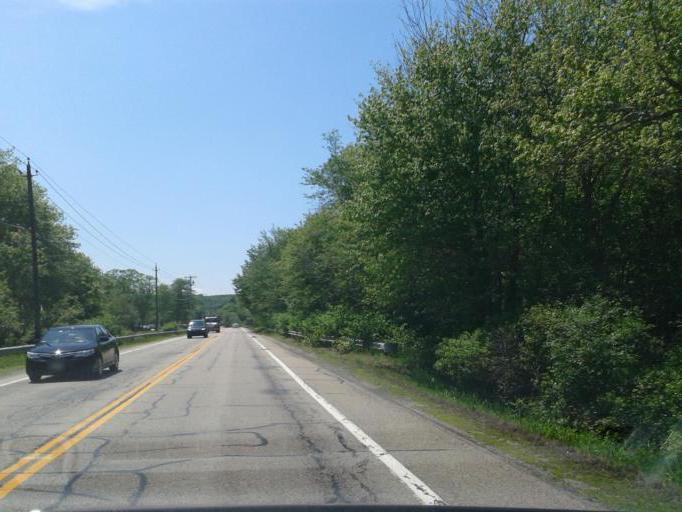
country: US
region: Rhode Island
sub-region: Washington County
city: Kingston
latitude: 41.4920
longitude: -71.4783
